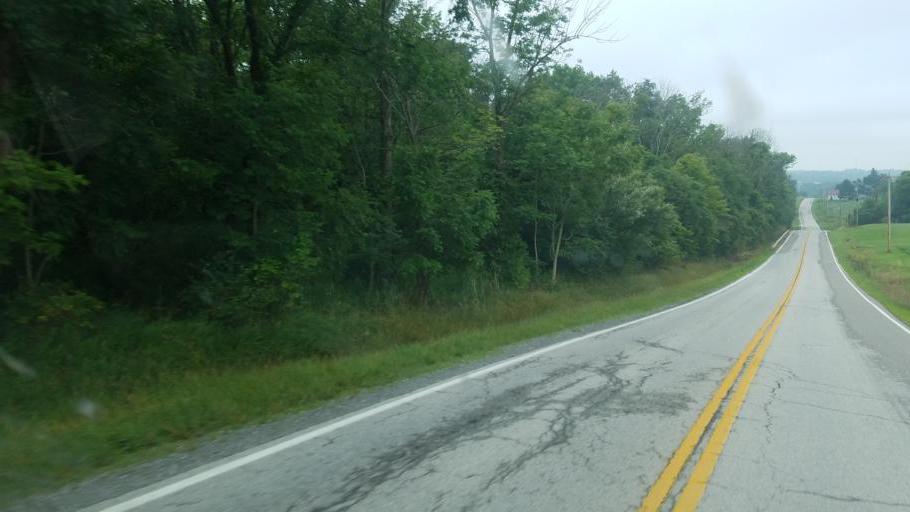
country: US
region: Ohio
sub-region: Highland County
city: Hillsboro
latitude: 39.2409
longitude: -83.5685
